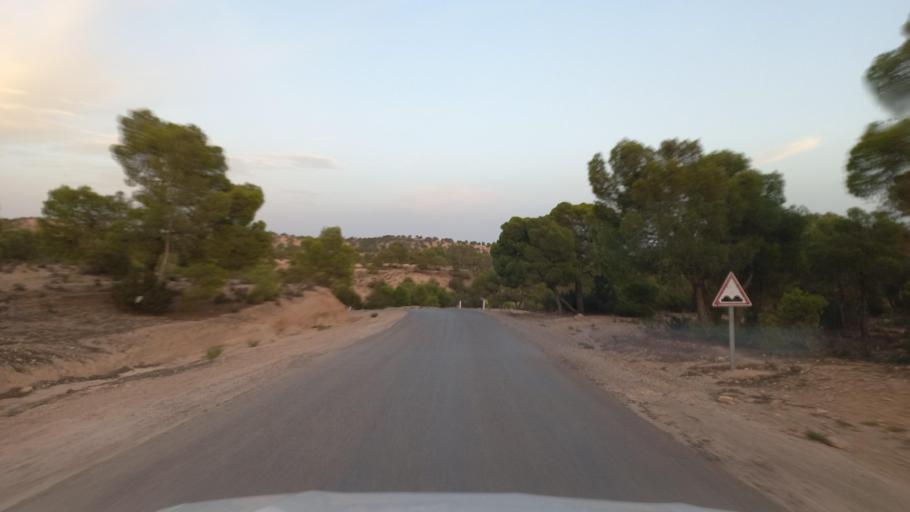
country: TN
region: Al Qasrayn
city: Sbiba
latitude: 35.4089
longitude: 8.9497
